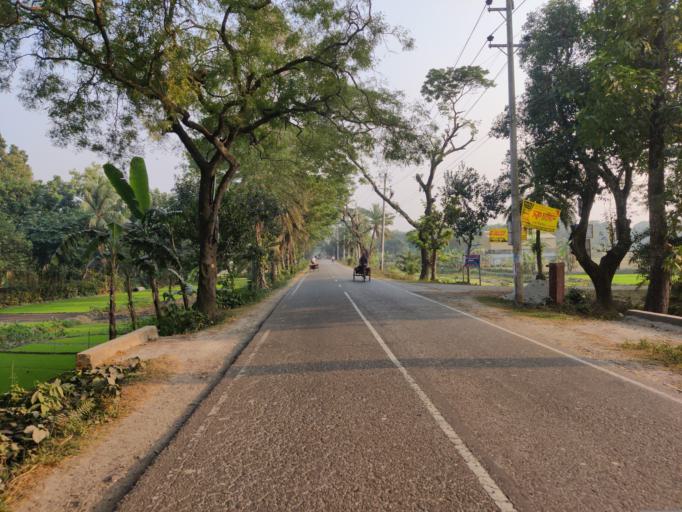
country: BD
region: Dhaka
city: Narsingdi
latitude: 24.0922
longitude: 90.7244
